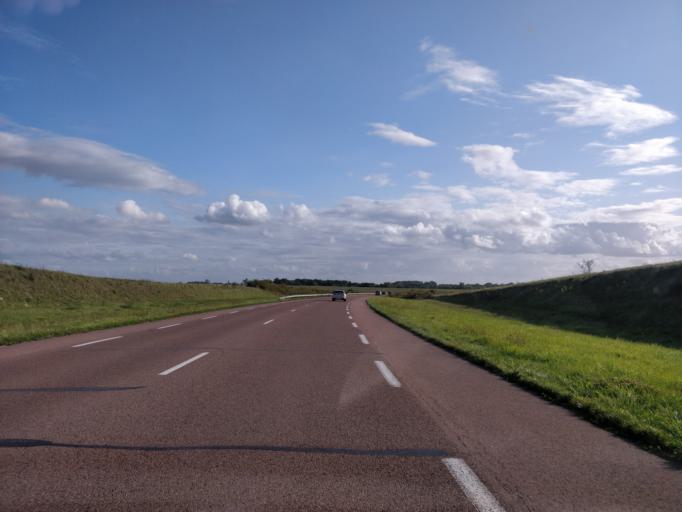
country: FR
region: Champagne-Ardenne
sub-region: Departement de l'Aube
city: Saint-Parres-aux-Tertres
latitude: 48.2900
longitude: 4.1395
